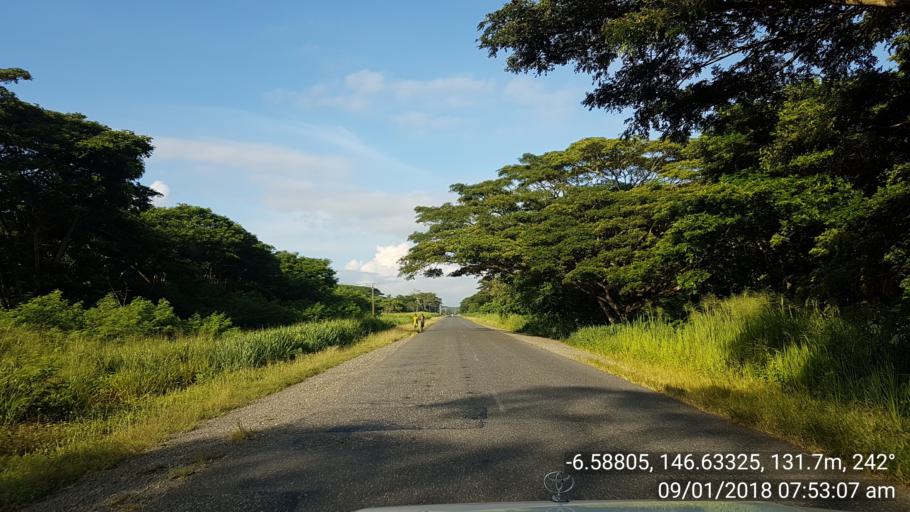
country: PG
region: Morobe
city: Lae
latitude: -6.5881
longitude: 146.6337
